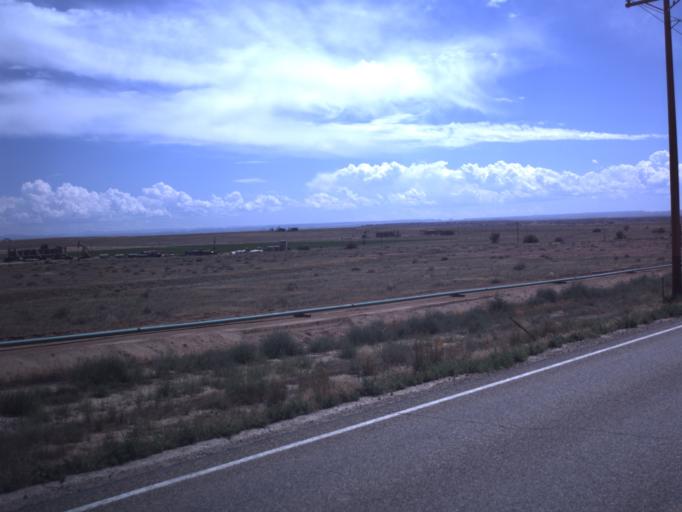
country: US
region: Utah
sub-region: Uintah County
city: Naples
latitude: 40.1625
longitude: -109.6644
